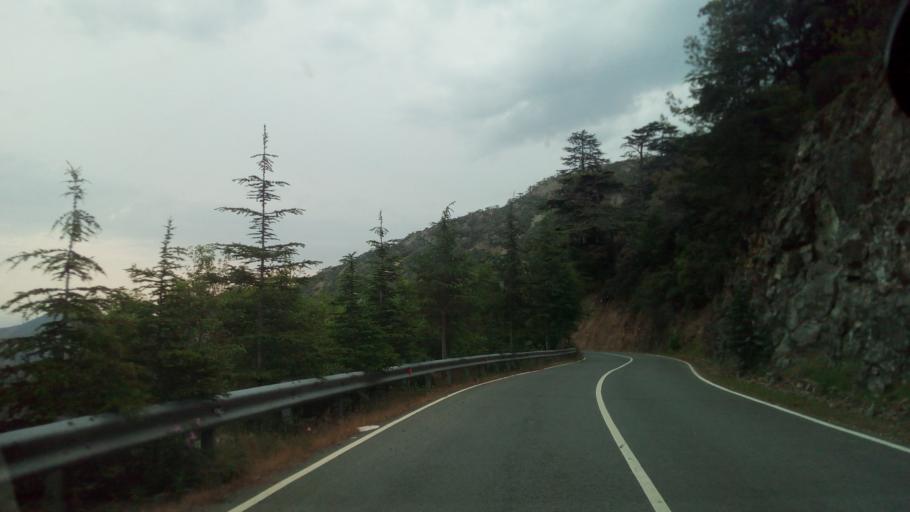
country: CY
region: Lefkosia
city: Kato Pyrgos
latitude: 35.0034
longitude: 32.6815
